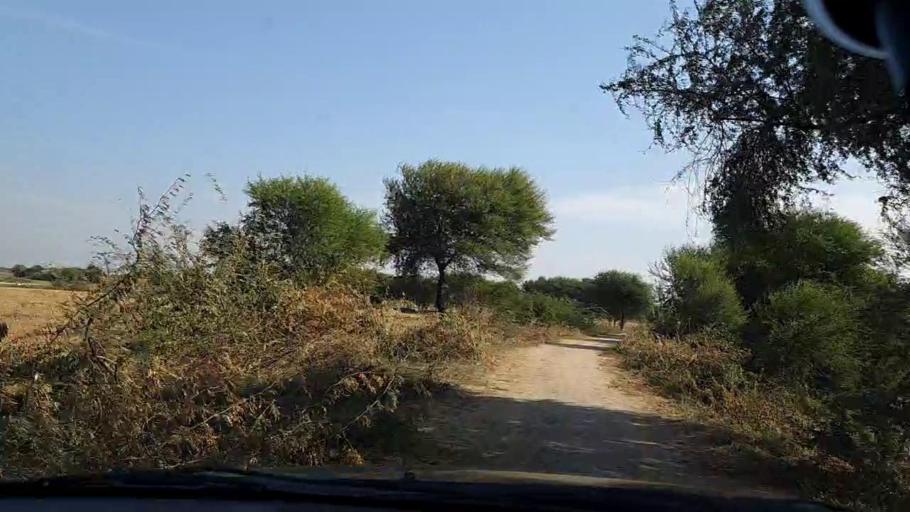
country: PK
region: Sindh
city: Mirpur Batoro
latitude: 24.6317
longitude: 68.2638
